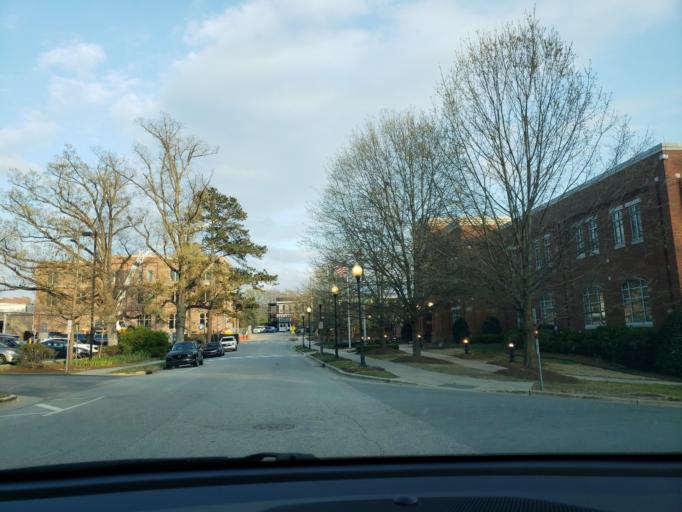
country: US
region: North Carolina
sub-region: Wake County
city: Apex
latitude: 35.7323
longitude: -78.8524
